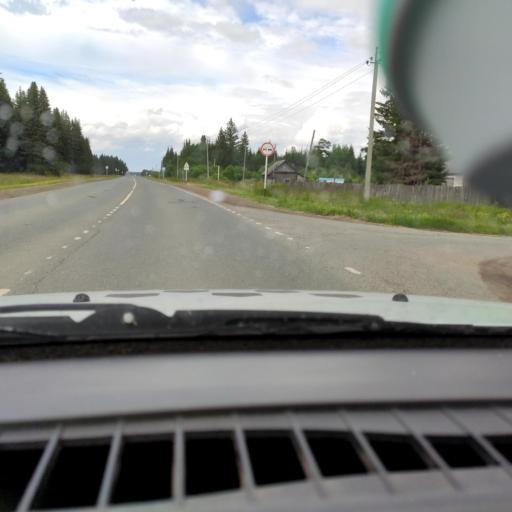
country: RU
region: Perm
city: Orda
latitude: 57.2002
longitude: 56.9181
